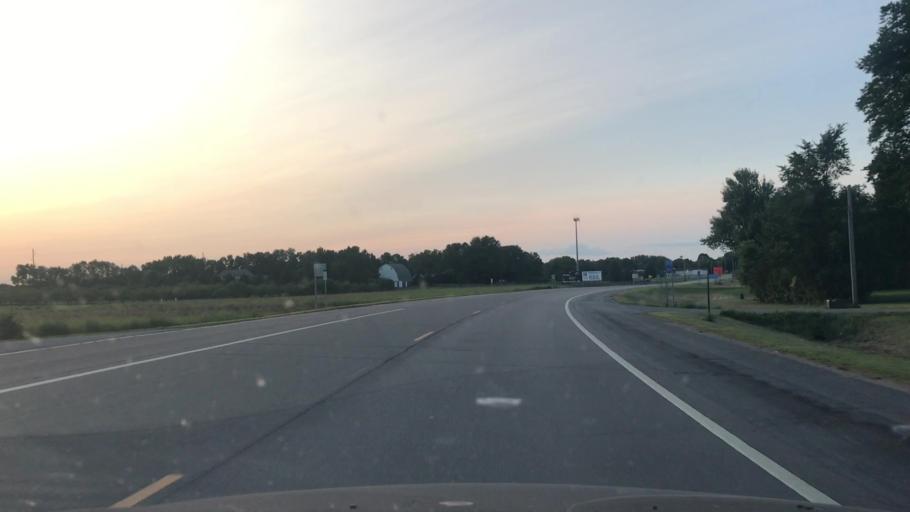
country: US
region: Minnesota
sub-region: Redwood County
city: Redwood Falls
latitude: 44.5257
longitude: -95.1191
